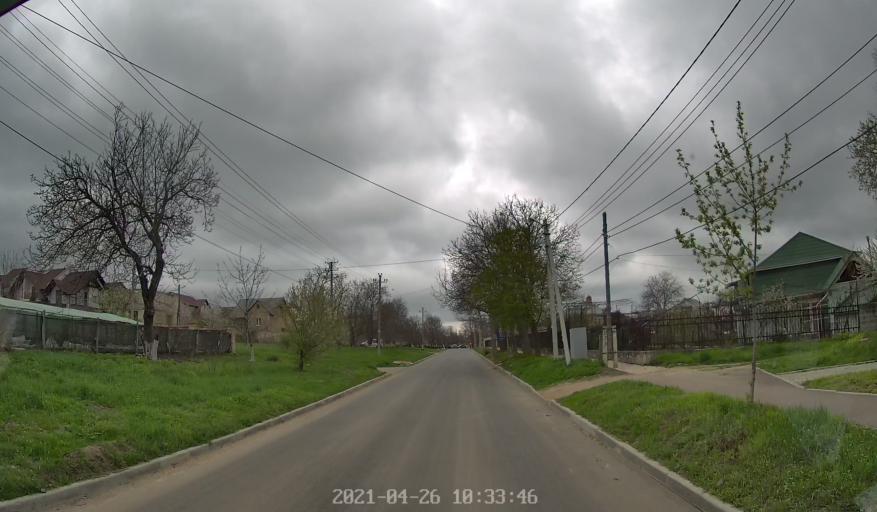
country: MD
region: Chisinau
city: Cricova
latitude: 47.1293
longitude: 28.8630
